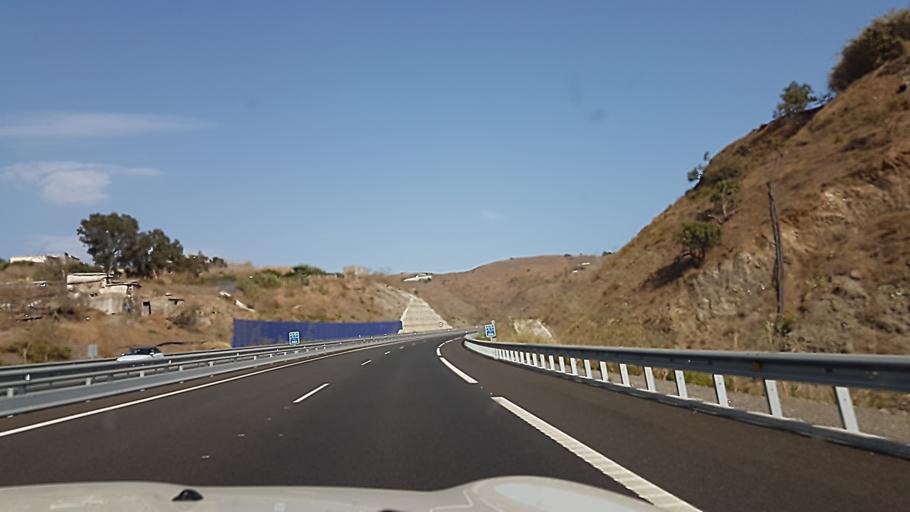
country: ES
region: Andalusia
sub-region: Provincia de Granada
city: Albunol
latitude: 36.7559
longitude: -3.2256
